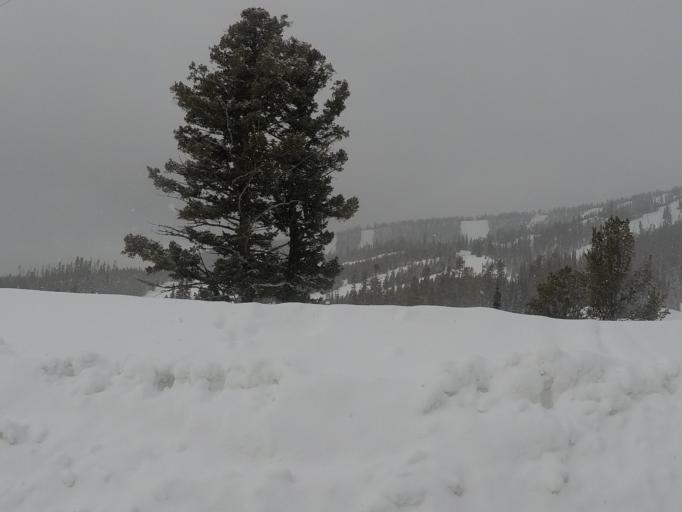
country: US
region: Montana
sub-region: Meagher County
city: White Sulphur Springs
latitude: 46.8385
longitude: -110.6996
